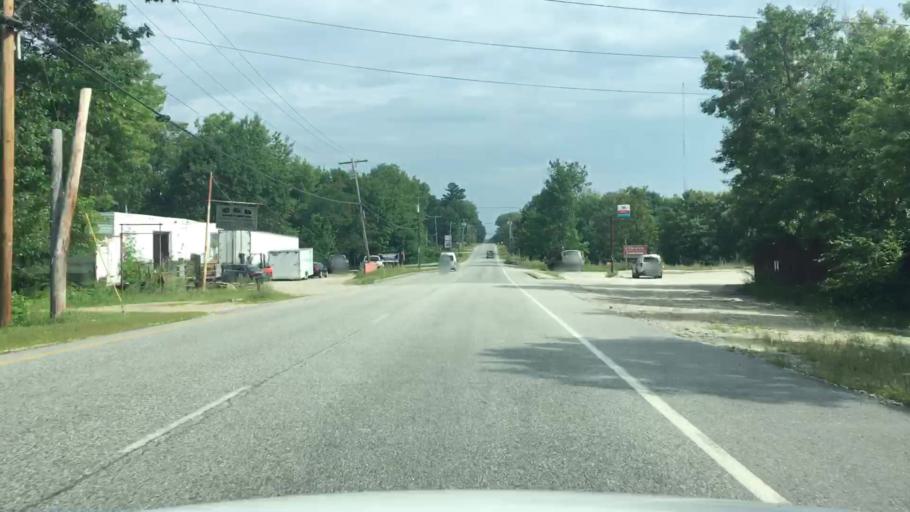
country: US
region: Maine
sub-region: Androscoggin County
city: Auburn
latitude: 44.0605
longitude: -70.2524
